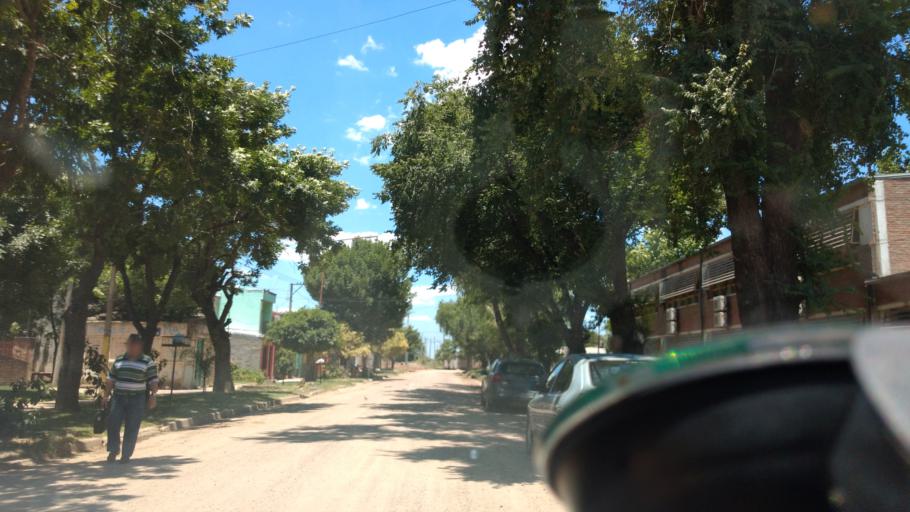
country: AR
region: Santa Fe
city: Laguna Paiva
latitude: -31.3119
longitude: -60.6634
